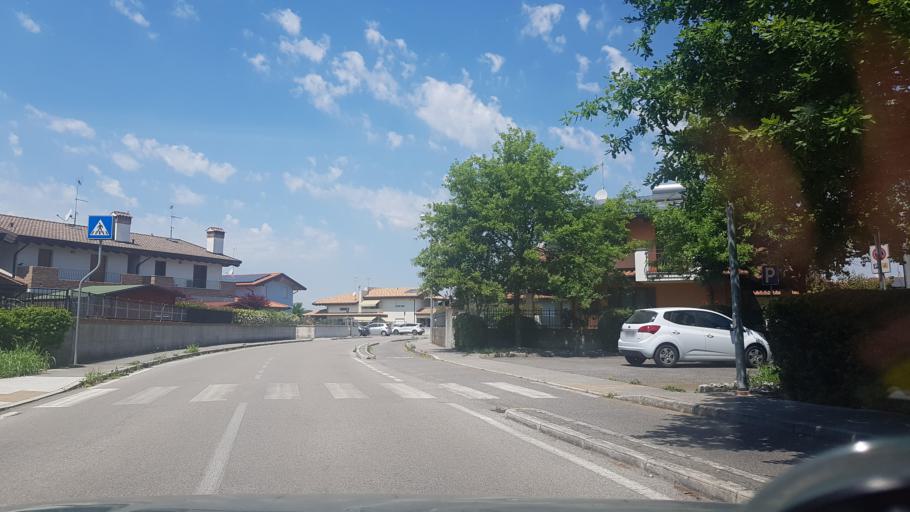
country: IT
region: Friuli Venezia Giulia
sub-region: Provincia di Gorizia
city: Turriaco
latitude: 45.8179
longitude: 13.4437
